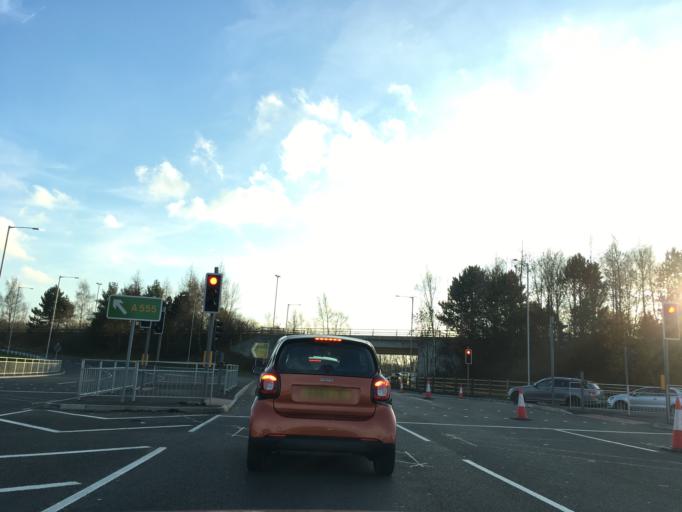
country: GB
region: England
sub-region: Borough of Stockport
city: Cheadle Hulme
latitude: 53.3566
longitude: -2.1994
